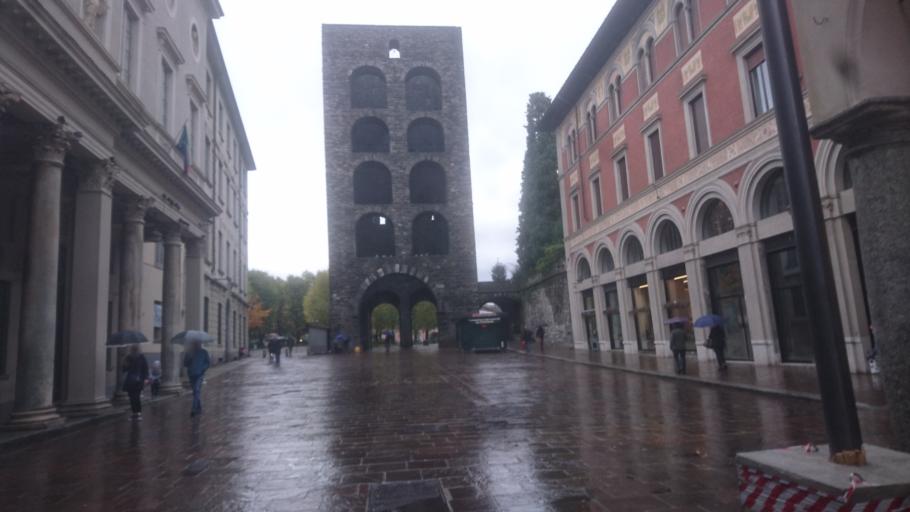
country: IT
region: Lombardy
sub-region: Provincia di Como
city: Como
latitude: 45.8072
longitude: 9.0850
